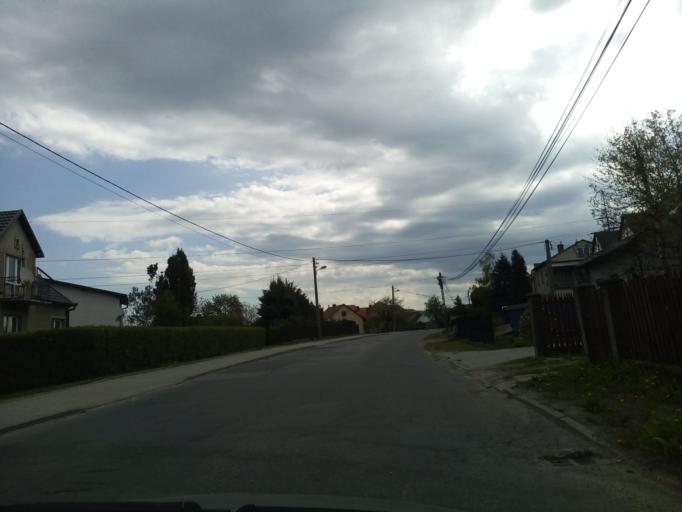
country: PL
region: Lesser Poland Voivodeship
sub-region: Powiat nowosadecki
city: Nowy Sacz
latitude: 49.5913
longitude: 20.7090
